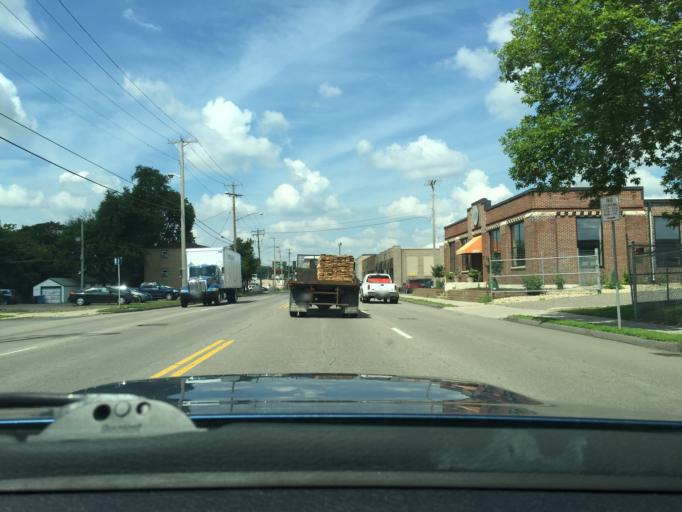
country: US
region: Minnesota
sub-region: Ramsey County
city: Lauderdale
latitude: 44.9916
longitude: -93.2147
